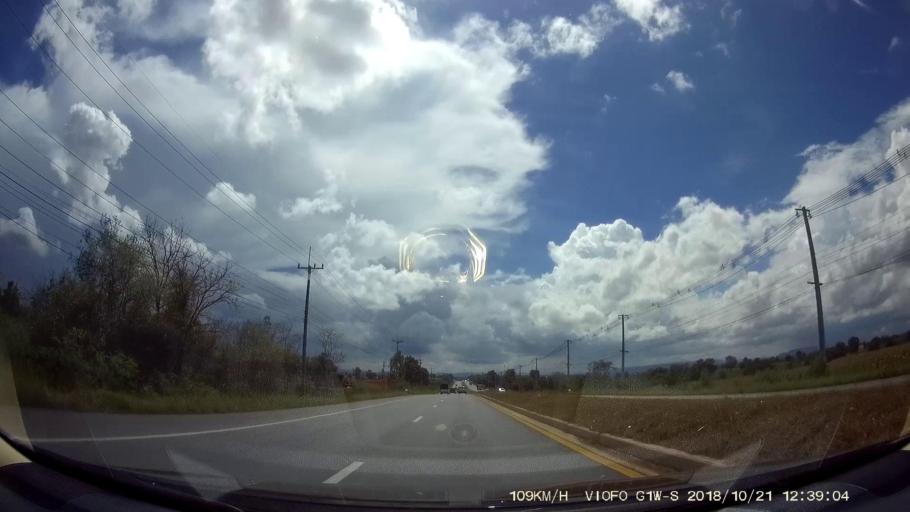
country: TH
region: Nakhon Ratchasima
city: Amphoe Sikhiu
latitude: 15.0441
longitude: 101.7025
